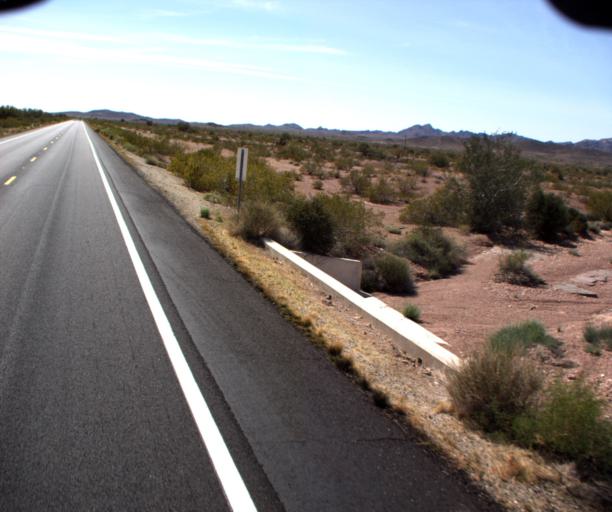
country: US
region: Arizona
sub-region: La Paz County
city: Quartzsite
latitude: 33.2842
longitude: -114.2293
